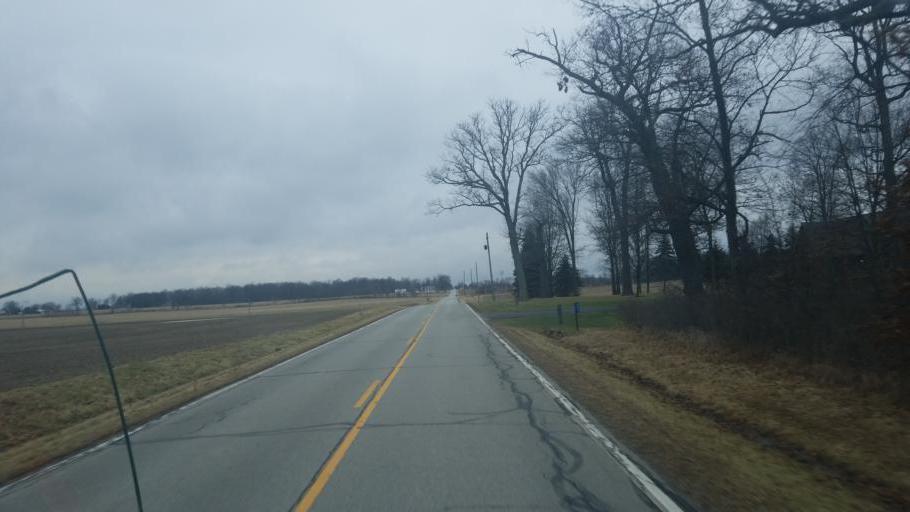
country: US
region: Ohio
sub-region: Crawford County
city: Bucyrus
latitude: 40.7372
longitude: -82.9533
